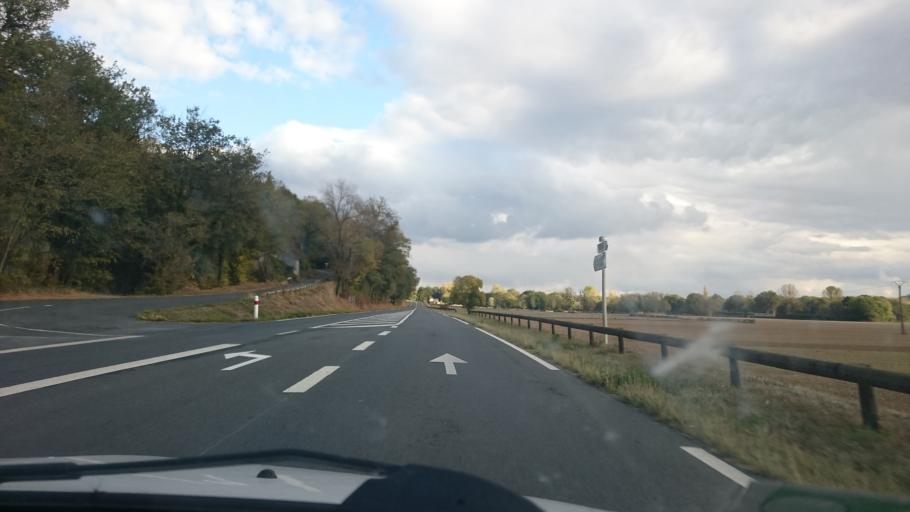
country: FR
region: Centre
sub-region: Departement de l'Indre
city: Saint-Gaultier
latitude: 46.6326
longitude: 1.4581
